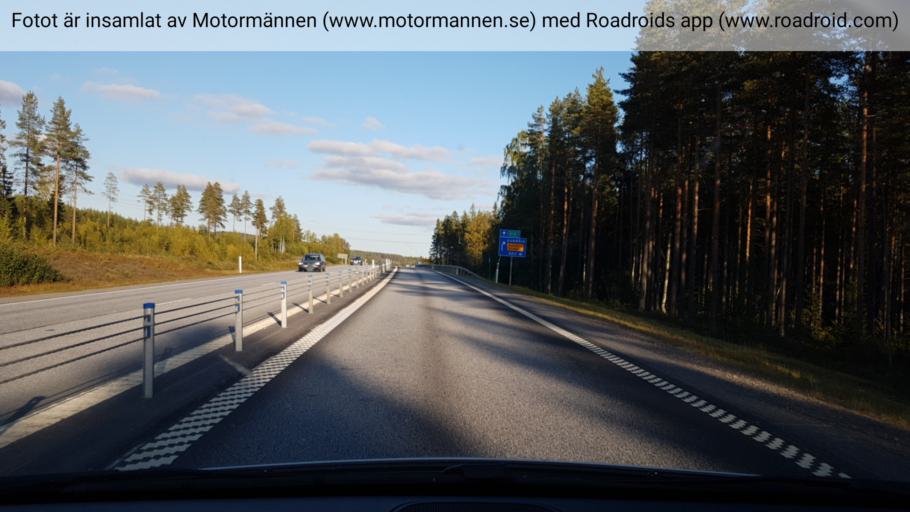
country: SE
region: Vaesterbotten
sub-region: Vannas Kommun
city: Vannasby
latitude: 63.8945
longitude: 19.9357
